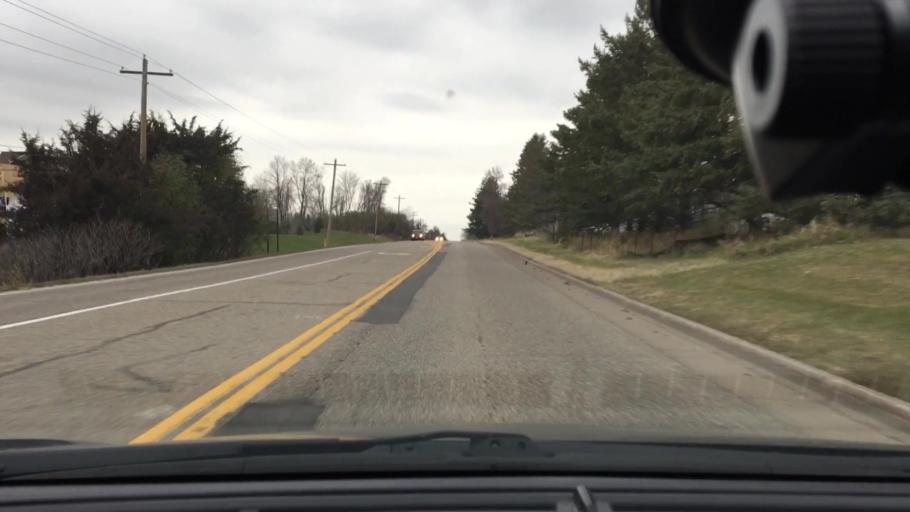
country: US
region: Minnesota
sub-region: Hennepin County
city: Corcoran
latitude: 45.0695
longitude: -93.5220
